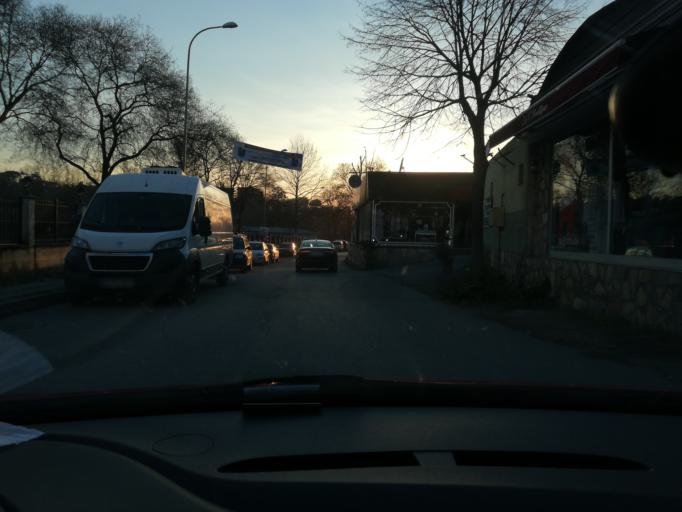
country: TR
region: Istanbul
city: Umraniye
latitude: 41.0812
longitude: 29.0780
